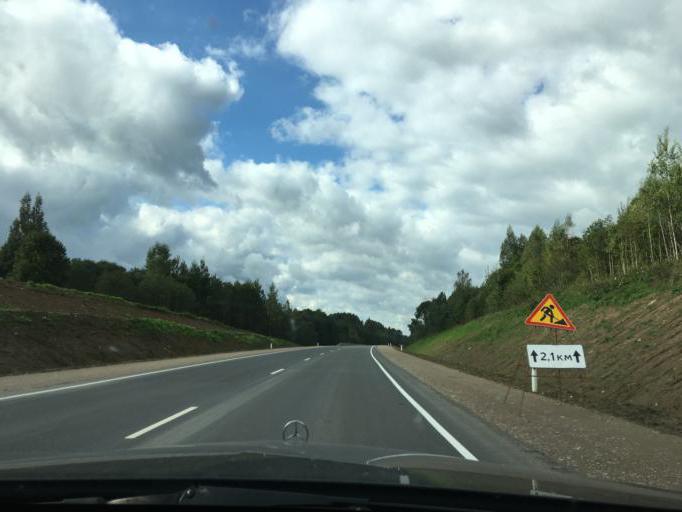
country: RU
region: Tverskaya
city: Toropets
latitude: 56.3118
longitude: 31.1503
